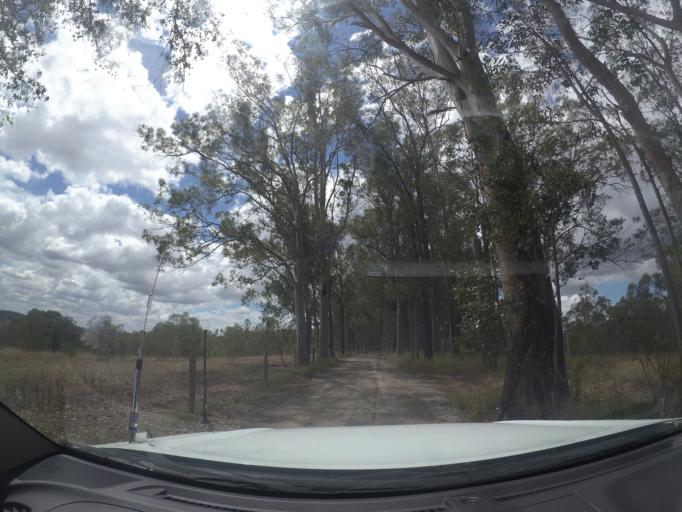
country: AU
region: Queensland
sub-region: Logan
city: Cedar Vale
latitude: -27.9135
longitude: 153.0310
